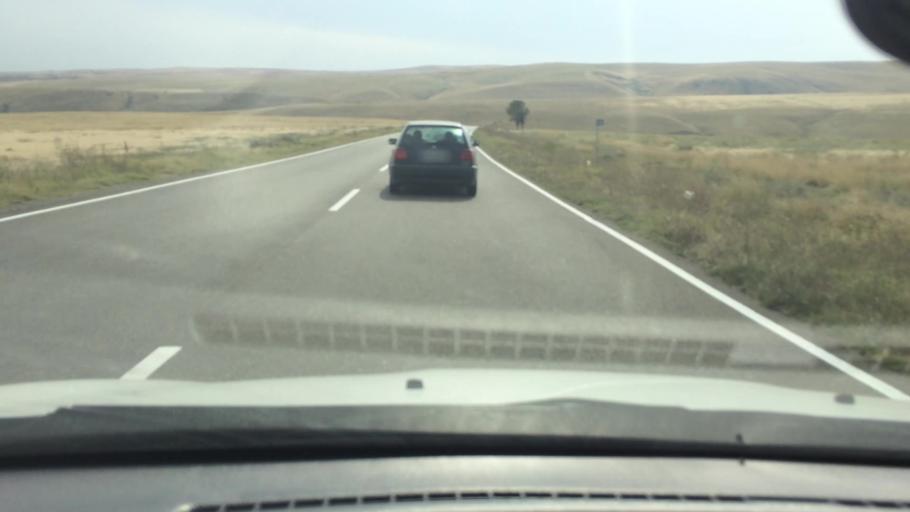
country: GE
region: Kvemo Kartli
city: Rust'avi
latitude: 41.5273
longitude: 44.9381
